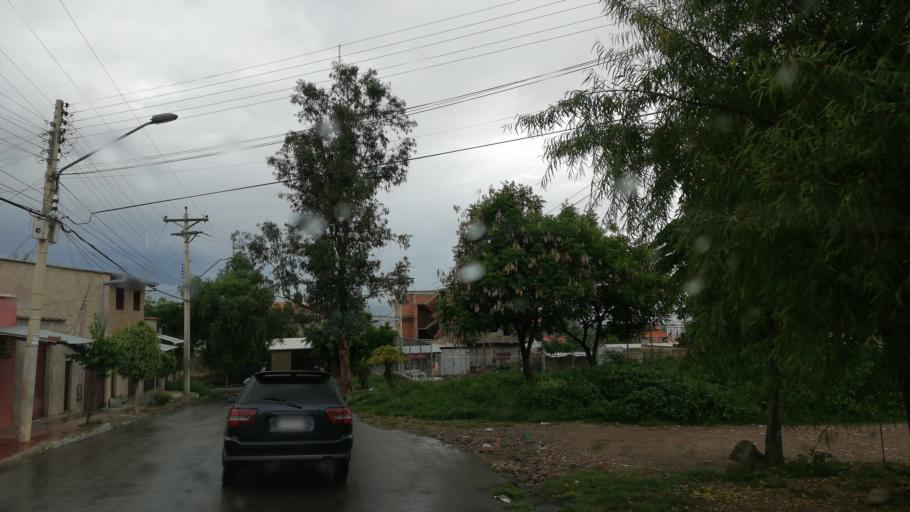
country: BO
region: Cochabamba
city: Cochabamba
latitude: -17.3484
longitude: -66.1773
